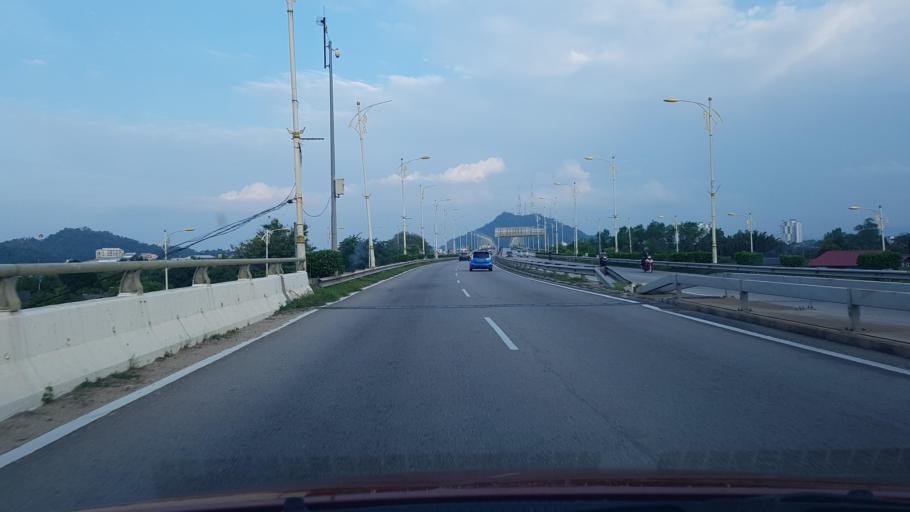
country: MY
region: Terengganu
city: Kuala Terengganu
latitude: 5.3291
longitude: 103.1218
